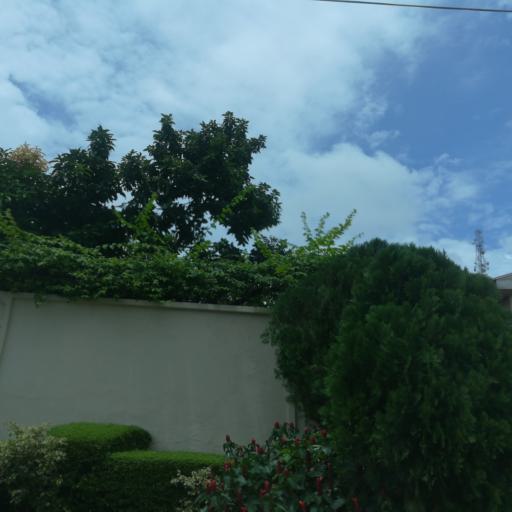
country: NG
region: Lagos
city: Ikoyi
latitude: 6.4412
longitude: 3.4650
